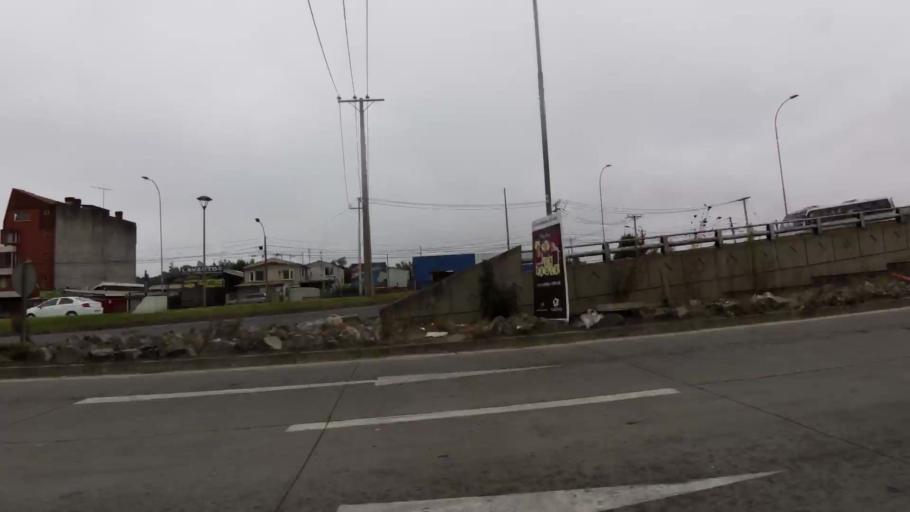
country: CL
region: Biobio
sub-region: Provincia de Concepcion
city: Concepcion
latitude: -36.8120
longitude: -73.0283
